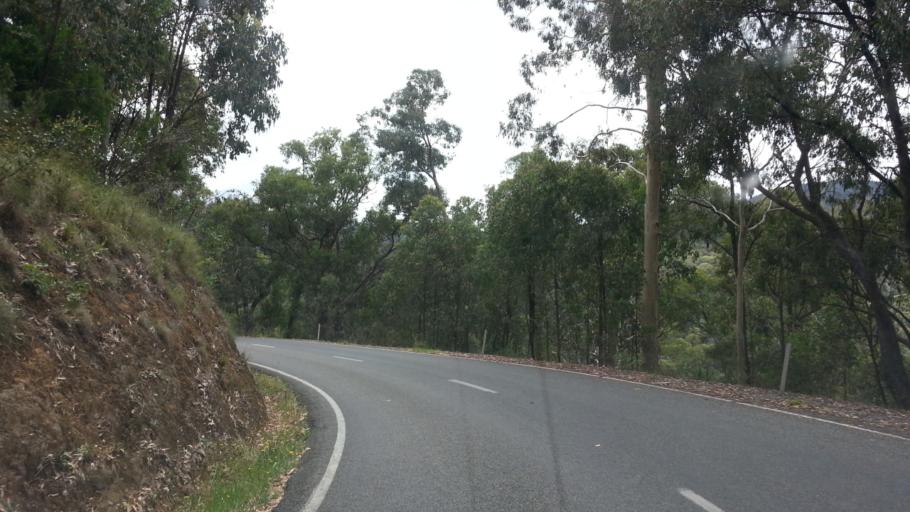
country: AU
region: Victoria
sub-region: Alpine
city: Mount Beauty
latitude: -36.7419
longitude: 147.1914
